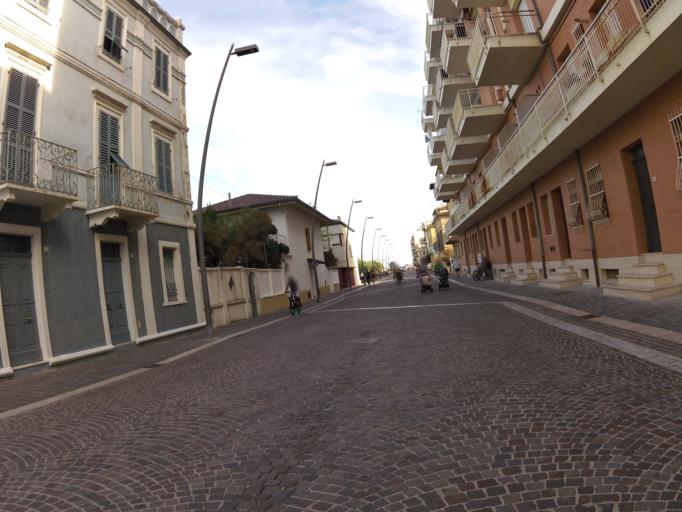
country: IT
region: The Marches
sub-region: Provincia di Macerata
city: Porto Recanati
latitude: 43.4304
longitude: 13.6668
